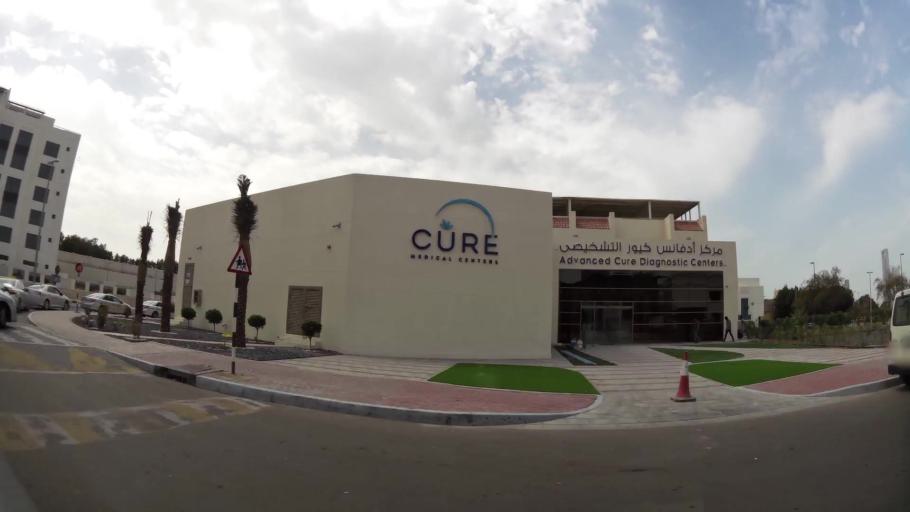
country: AE
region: Abu Dhabi
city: Abu Dhabi
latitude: 24.4586
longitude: 54.3499
